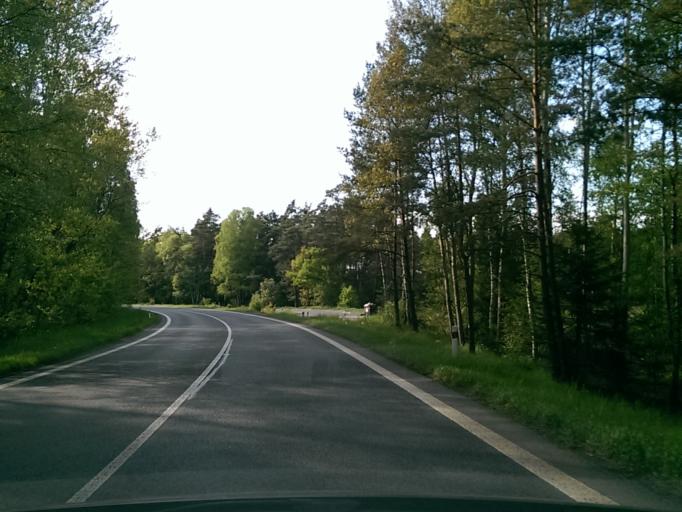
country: CZ
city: Doksy
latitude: 50.5401
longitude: 14.6799
